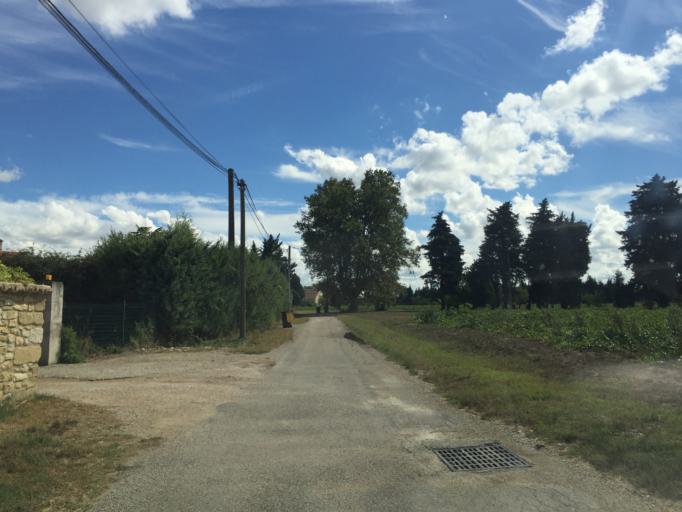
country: FR
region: Provence-Alpes-Cote d'Azur
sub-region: Departement du Vaucluse
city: Caderousse
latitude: 44.1261
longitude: 4.7341
